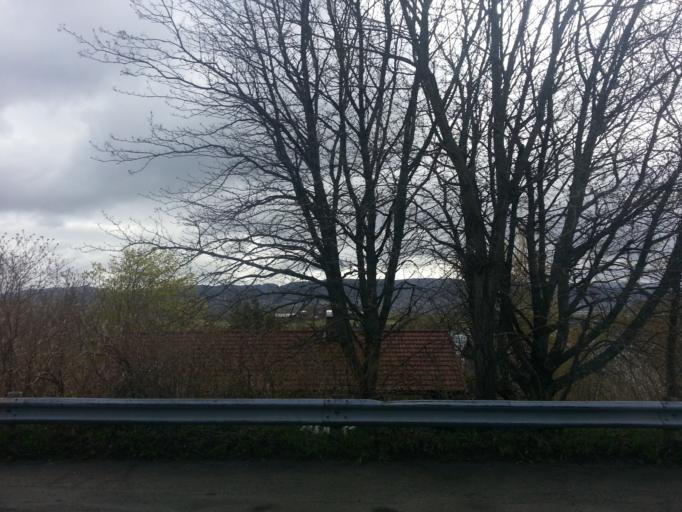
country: NO
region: Sor-Trondelag
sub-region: Trondheim
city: Trondheim
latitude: 63.4092
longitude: 10.3500
